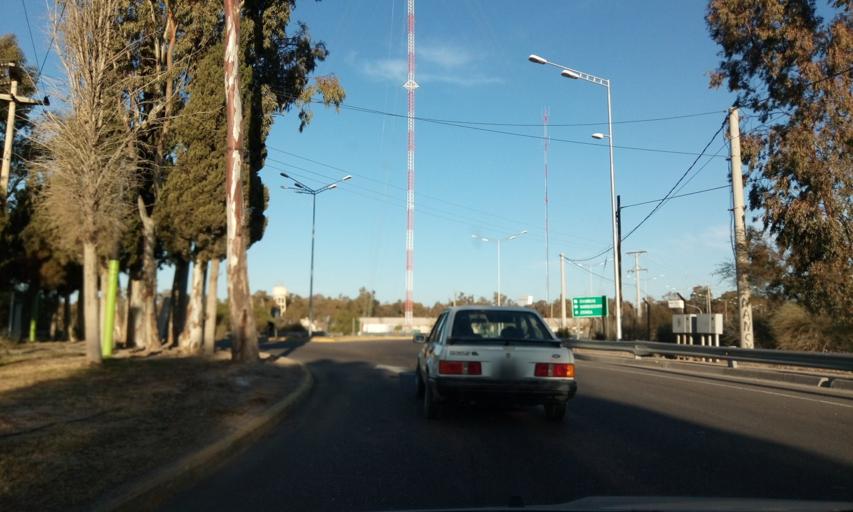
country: AR
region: San Juan
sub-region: Departamento de Rivadavia
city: Rivadavia
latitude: -31.5159
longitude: -68.6312
